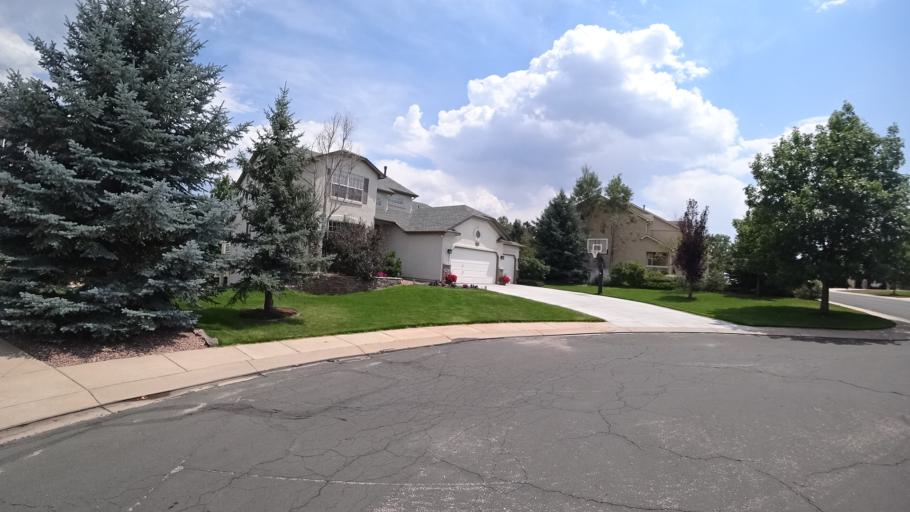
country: US
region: Colorado
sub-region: El Paso County
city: Black Forest
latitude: 38.9668
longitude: -104.7760
